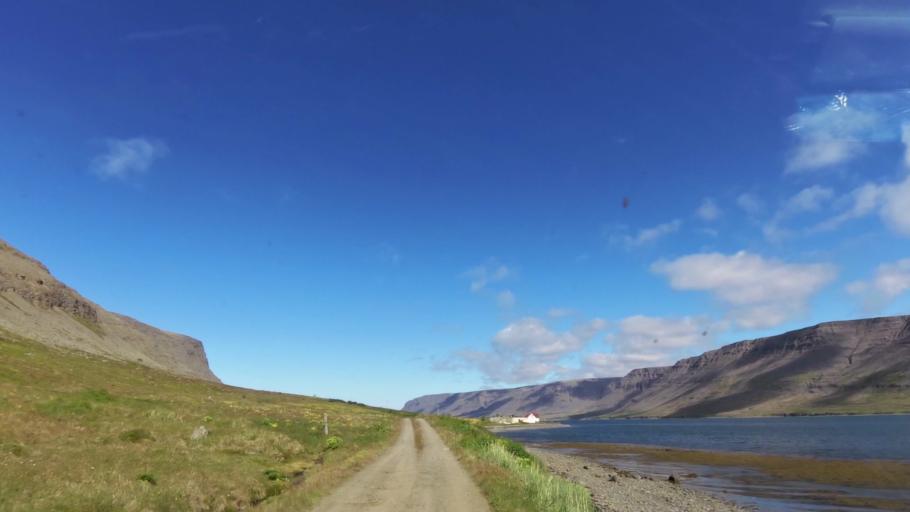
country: IS
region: West
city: Olafsvik
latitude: 65.6188
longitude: -23.8649
